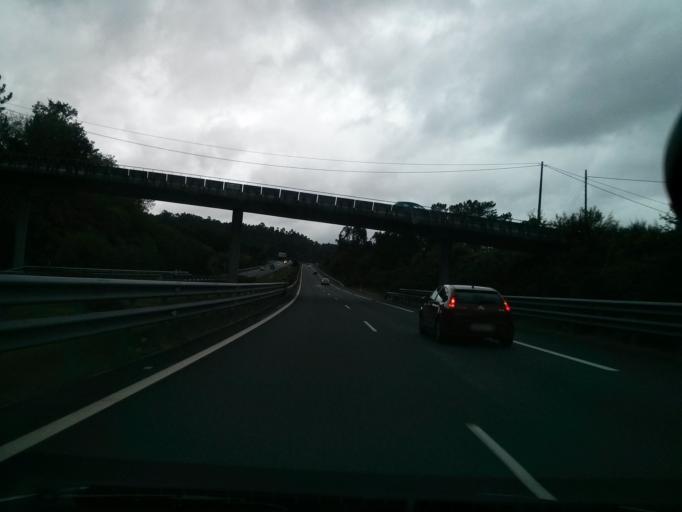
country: ES
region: Galicia
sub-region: Provincia de Pontevedra
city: Ponteareas
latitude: 42.1437
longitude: -8.4594
